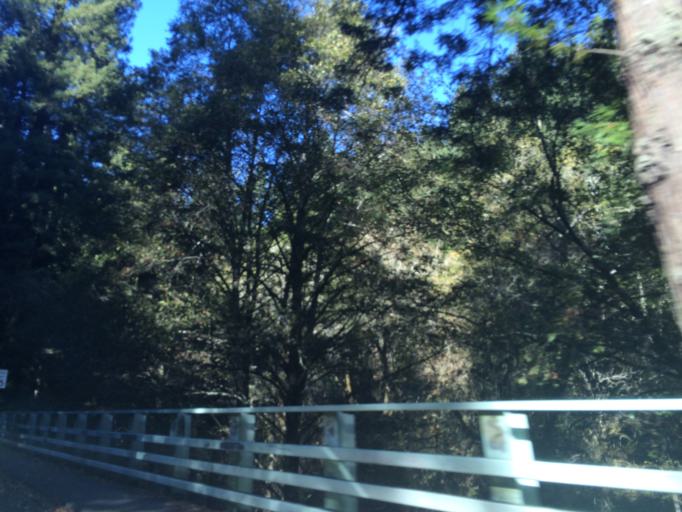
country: US
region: California
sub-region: Marin County
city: Lagunitas-Forest Knolls
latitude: 38.0046
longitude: -122.7091
